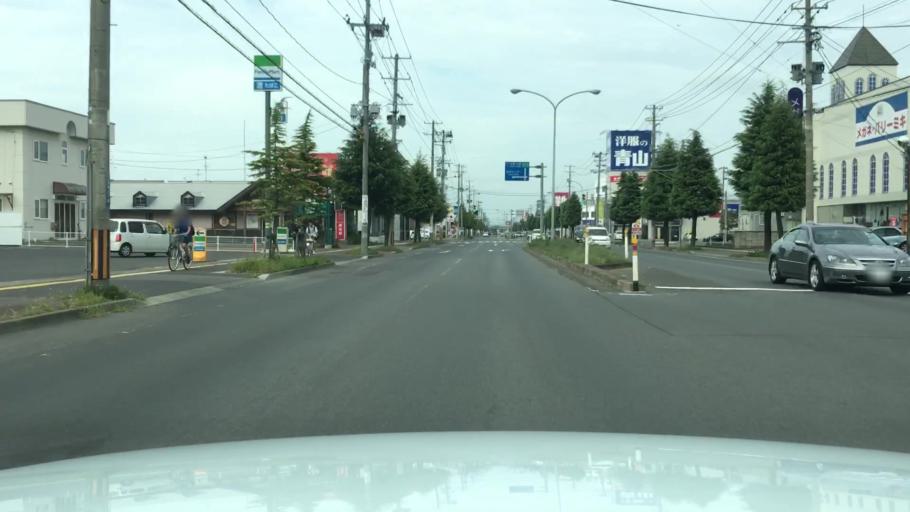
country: JP
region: Aomori
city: Hirosaki
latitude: 40.6135
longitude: 140.4833
